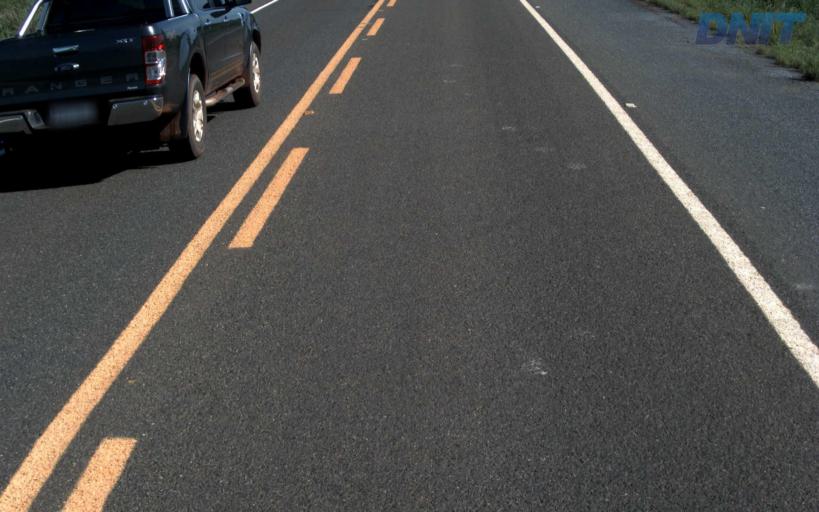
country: BR
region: Goias
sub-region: Sao Miguel Do Araguaia
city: Sao Miguel do Araguaia
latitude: -13.4563
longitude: -50.1190
